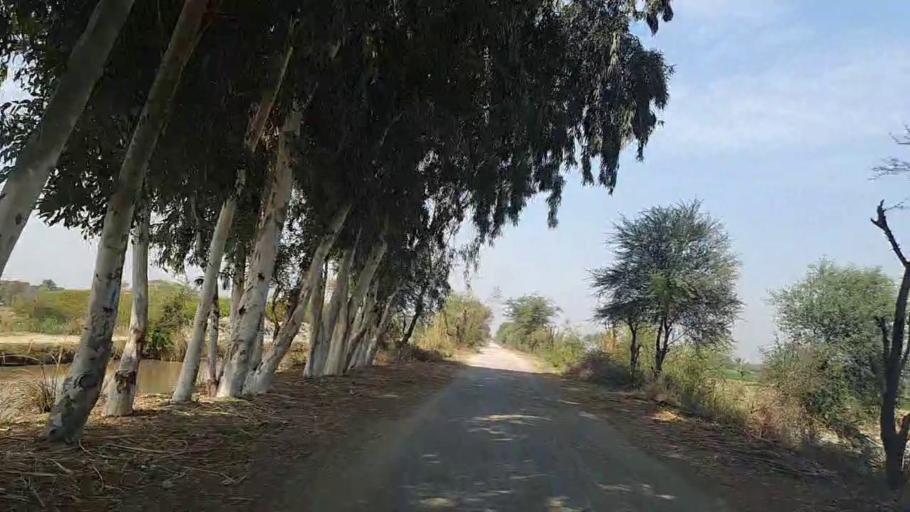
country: PK
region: Sindh
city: Mirpur Khas
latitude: 25.4881
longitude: 68.9233
